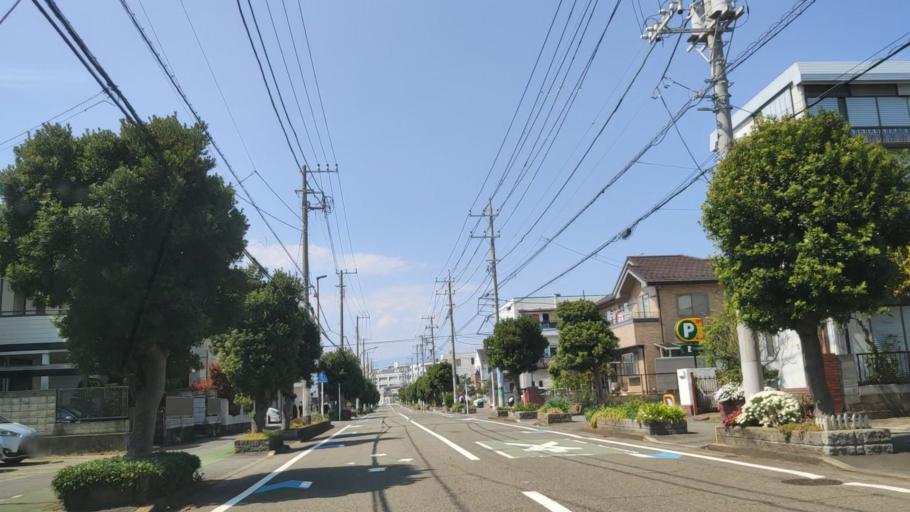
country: JP
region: Kanagawa
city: Hiratsuka
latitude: 35.3226
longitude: 139.3554
